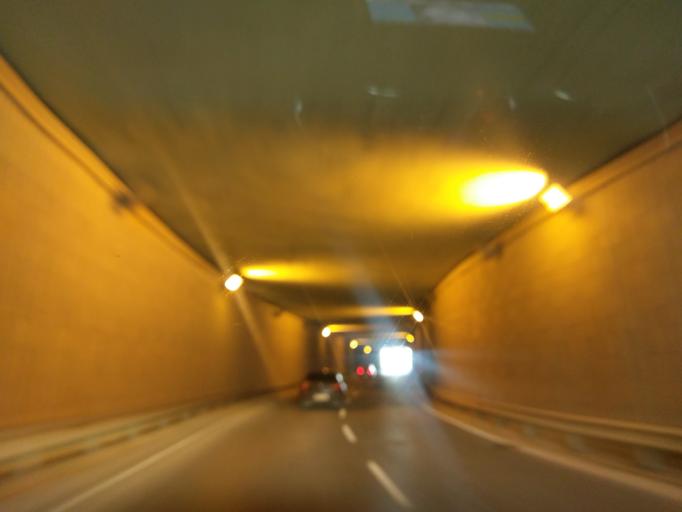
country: TR
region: Istanbul
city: Esenyurt
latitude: 41.0592
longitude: 28.6906
